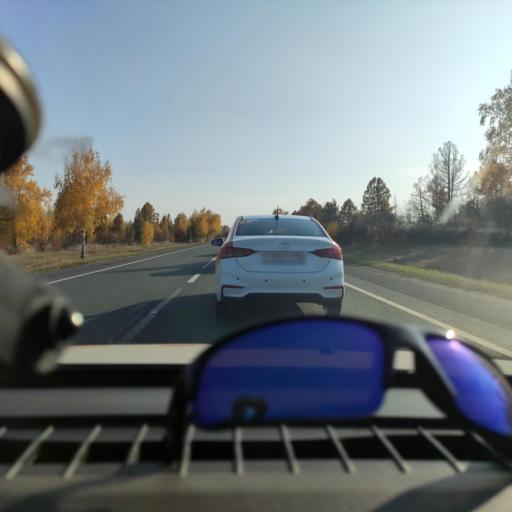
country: RU
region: Samara
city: Bereza
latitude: 53.4816
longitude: 50.1168
